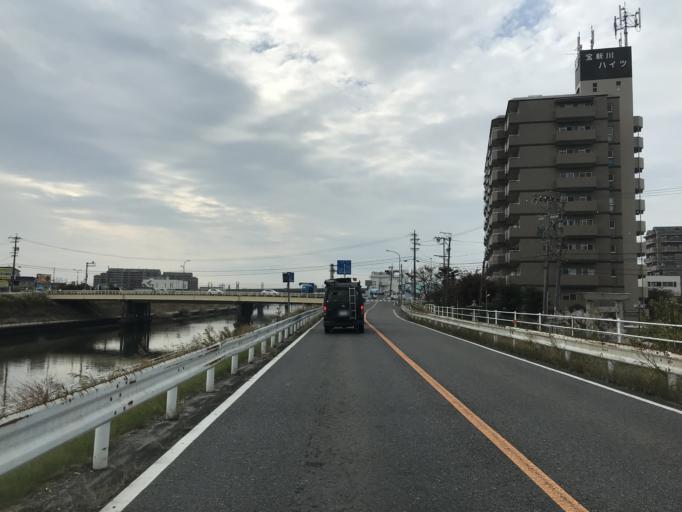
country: JP
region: Aichi
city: Nagoya-shi
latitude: 35.2067
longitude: 136.8586
